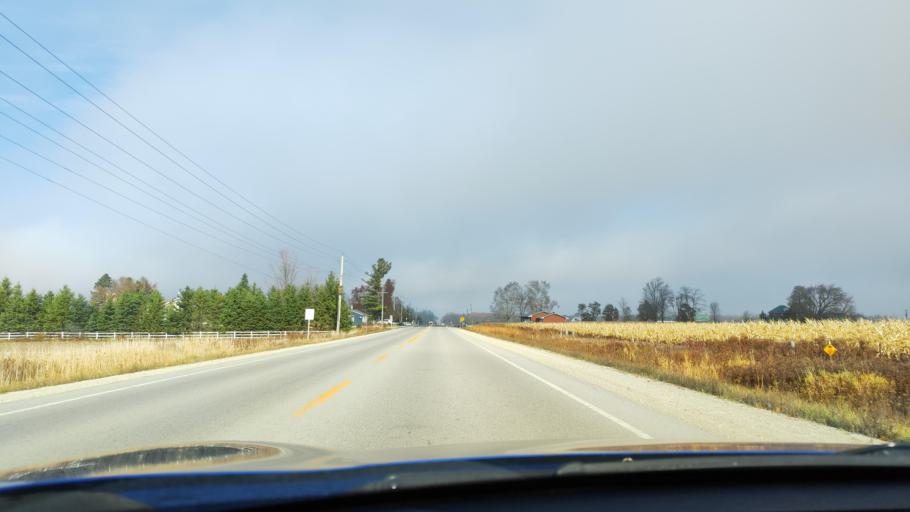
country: CA
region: Ontario
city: Wasaga Beach
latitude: 44.4534
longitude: -80.0715
